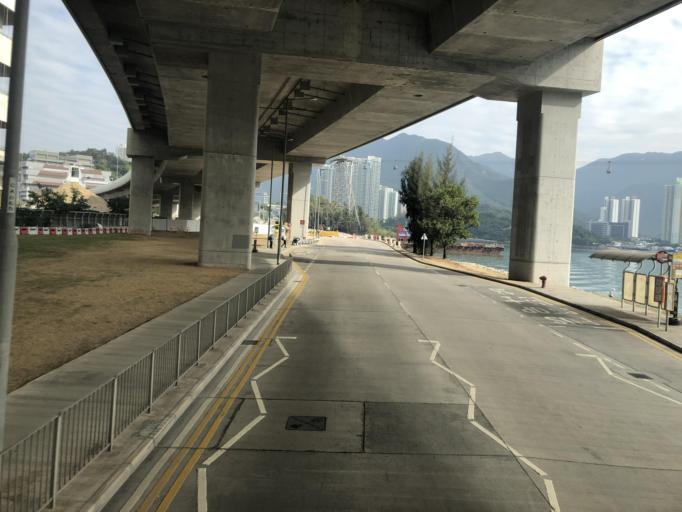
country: HK
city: Tai O
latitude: 22.2921
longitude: 113.9282
